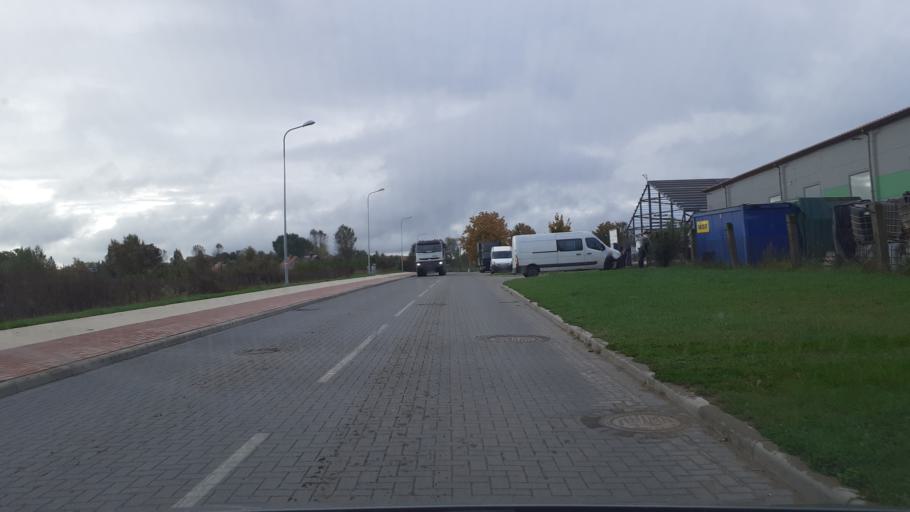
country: LV
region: Kuldigas Rajons
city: Kuldiga
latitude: 56.9818
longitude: 21.9492
